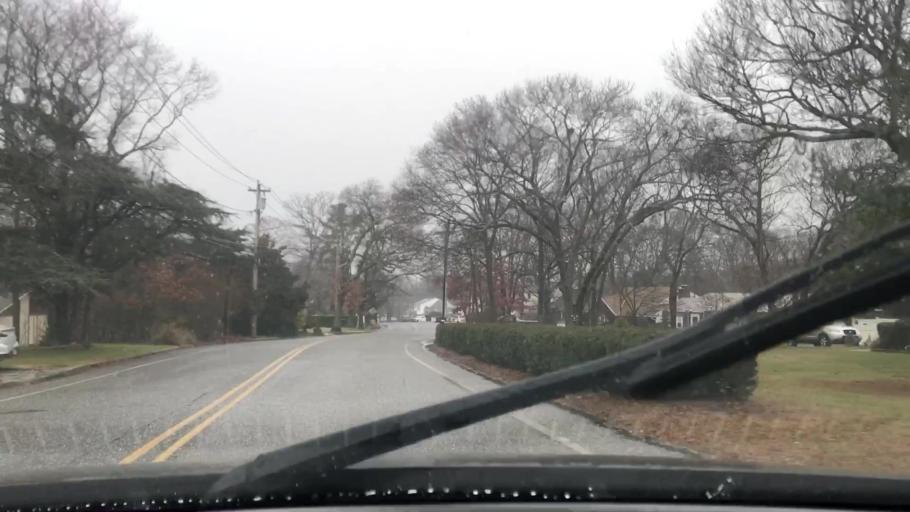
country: US
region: New York
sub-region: Suffolk County
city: Centereach
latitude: 40.8411
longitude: -73.0856
